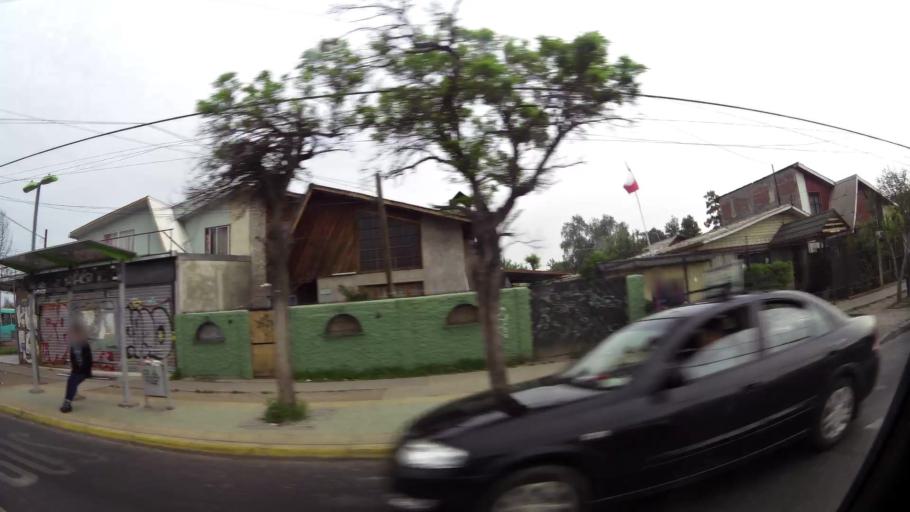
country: CL
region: Santiago Metropolitan
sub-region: Provincia de Santiago
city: Lo Prado
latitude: -33.5182
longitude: -70.7759
